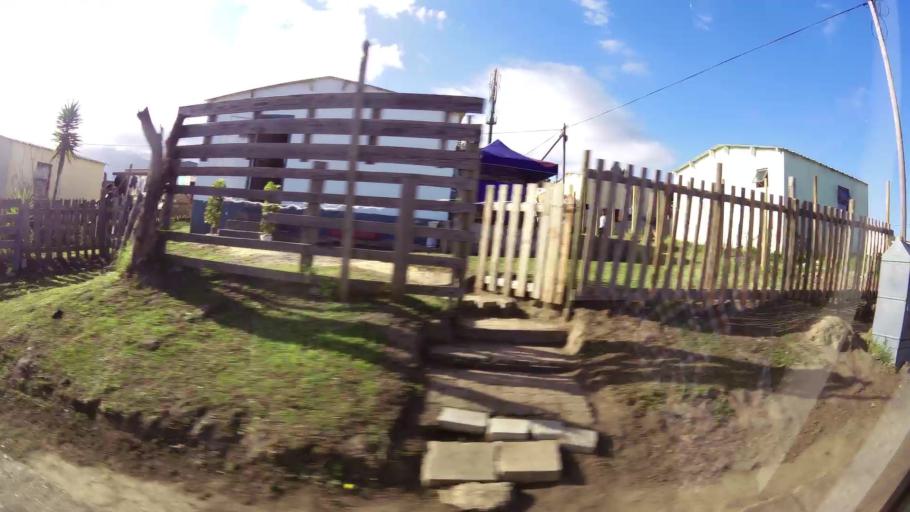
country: ZA
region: Western Cape
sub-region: Eden District Municipality
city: George
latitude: -33.9767
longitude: 22.4764
